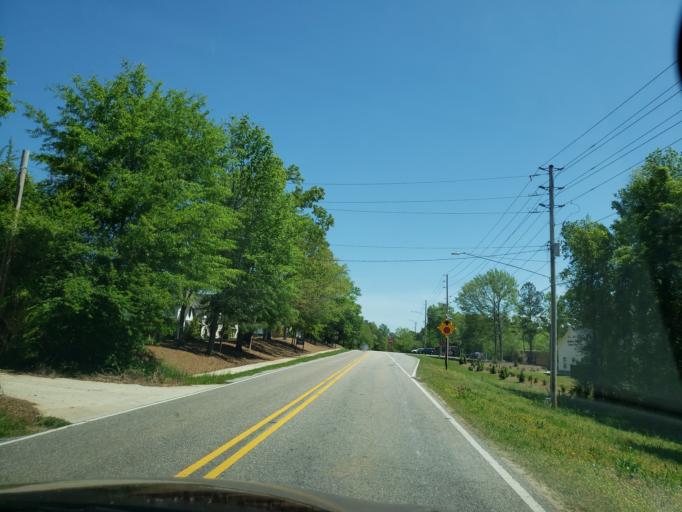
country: US
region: Alabama
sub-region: Lee County
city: Auburn
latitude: 32.6575
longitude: -85.5191
